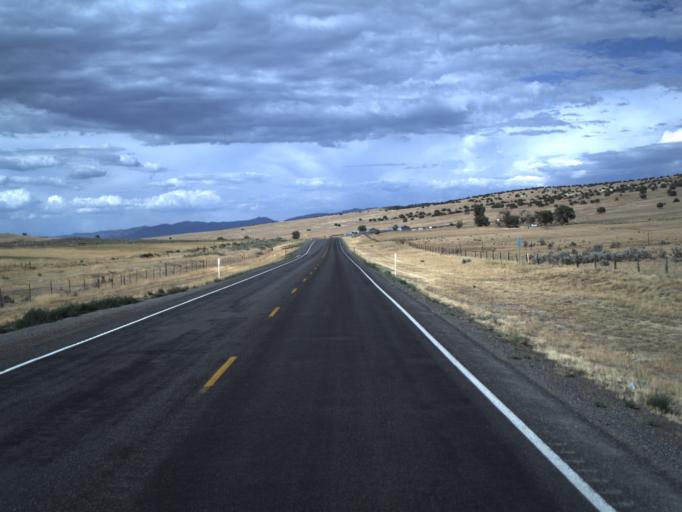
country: US
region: Utah
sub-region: Sanpete County
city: Ephraim
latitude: 39.4033
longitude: -111.5678
